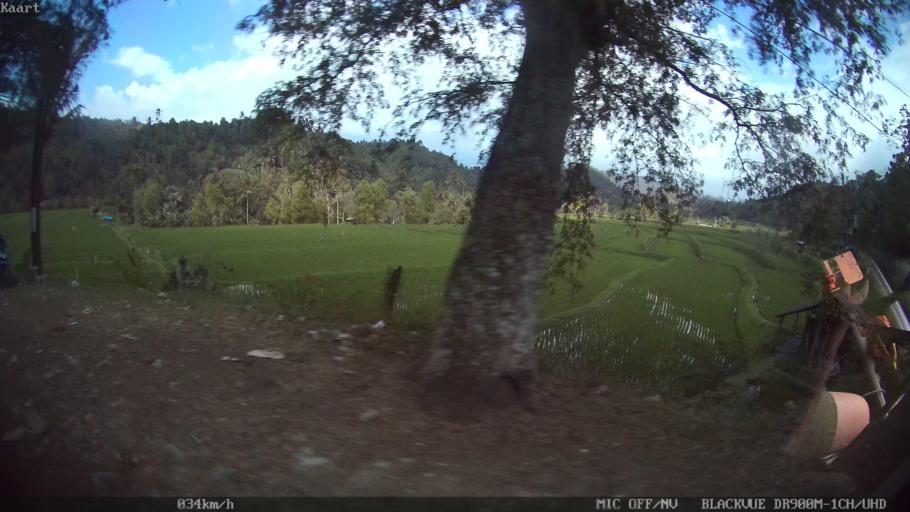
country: ID
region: Bali
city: Kauhan
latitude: -8.2774
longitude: 114.9701
